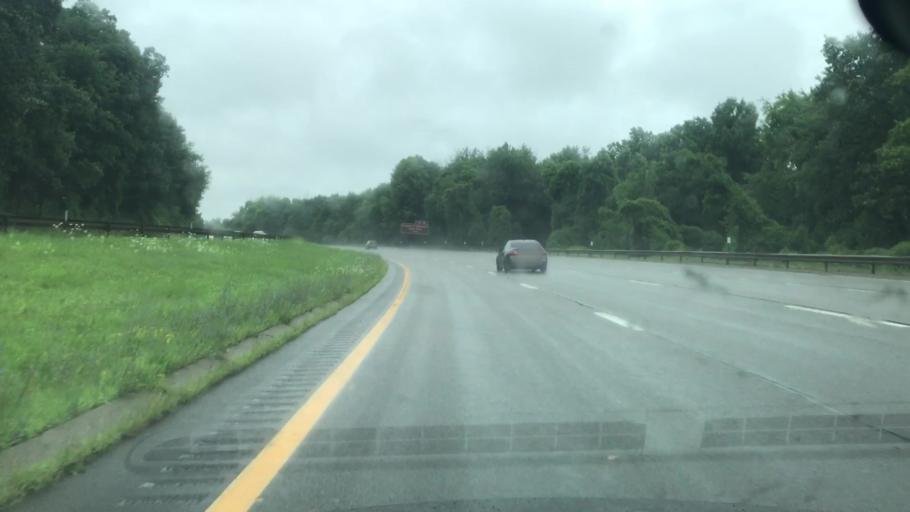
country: US
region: New York
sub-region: Westchester County
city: Yorktown Heights
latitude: 41.2703
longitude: -73.8068
